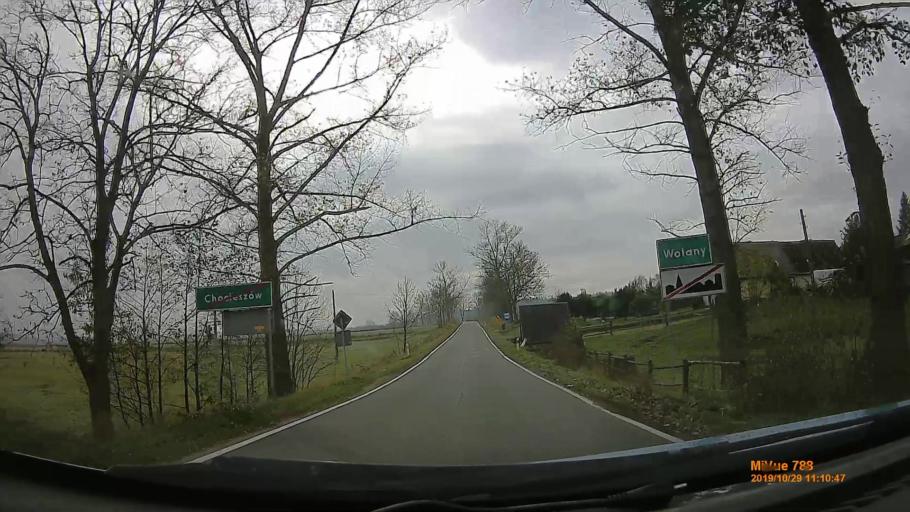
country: PL
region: Lower Silesian Voivodeship
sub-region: Powiat klodzki
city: Polanica-Zdroj
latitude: 50.4404
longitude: 16.5005
